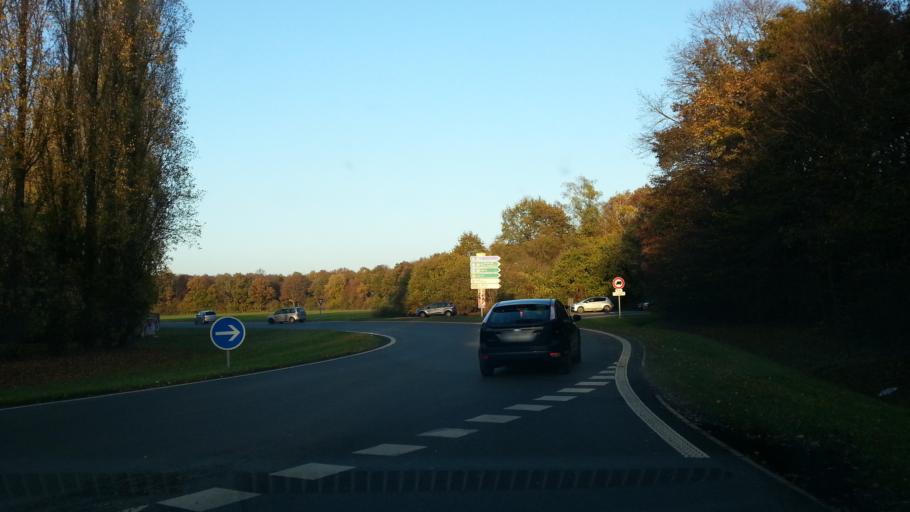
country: FR
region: Picardie
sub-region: Departement de l'Oise
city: Chantilly
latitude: 49.2053
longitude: 2.4623
